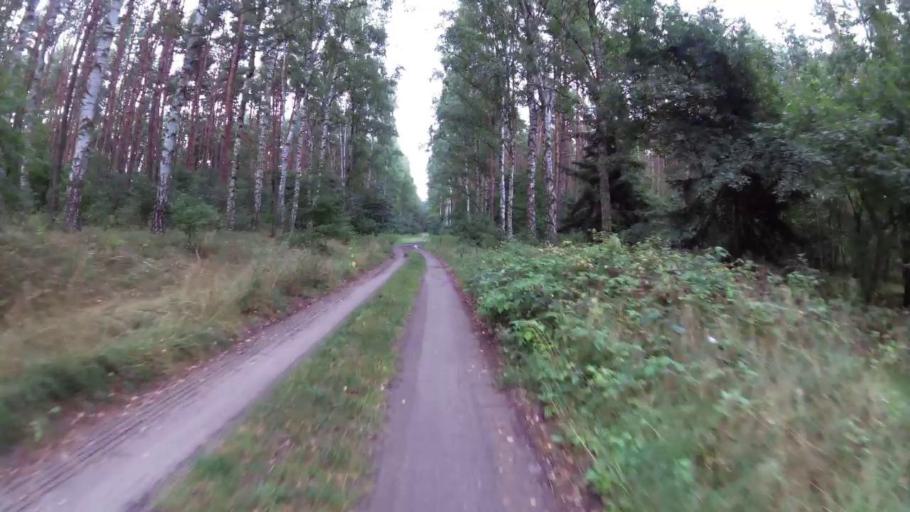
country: PL
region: West Pomeranian Voivodeship
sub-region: Powiat mysliborski
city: Debno
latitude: 52.7831
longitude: 14.7154
